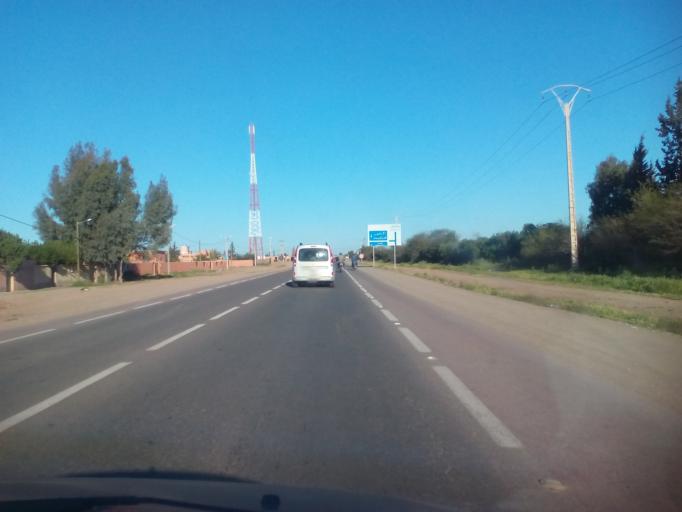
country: MA
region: Marrakech-Tensift-Al Haouz
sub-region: Marrakech
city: Marrakesh
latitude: 31.6307
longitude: -8.1686
